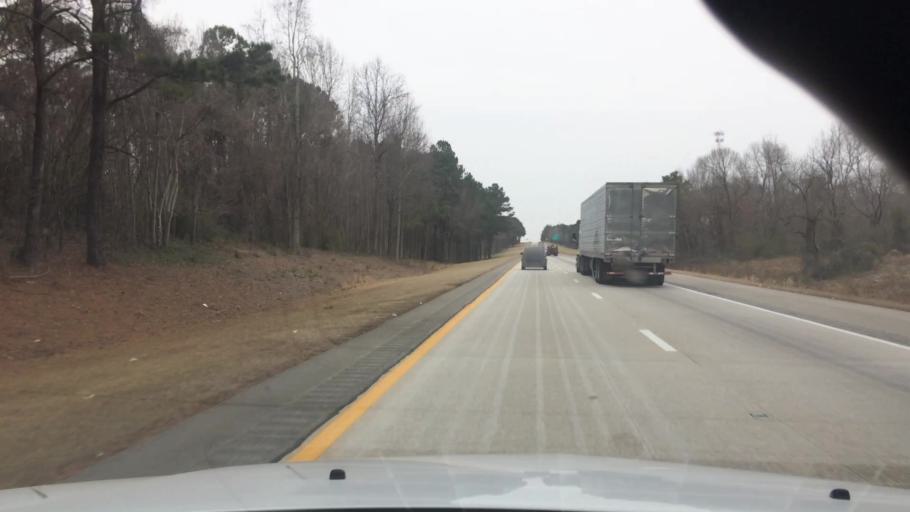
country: US
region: North Carolina
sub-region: Nash County
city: Nashville
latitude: 35.9529
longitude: -77.8890
